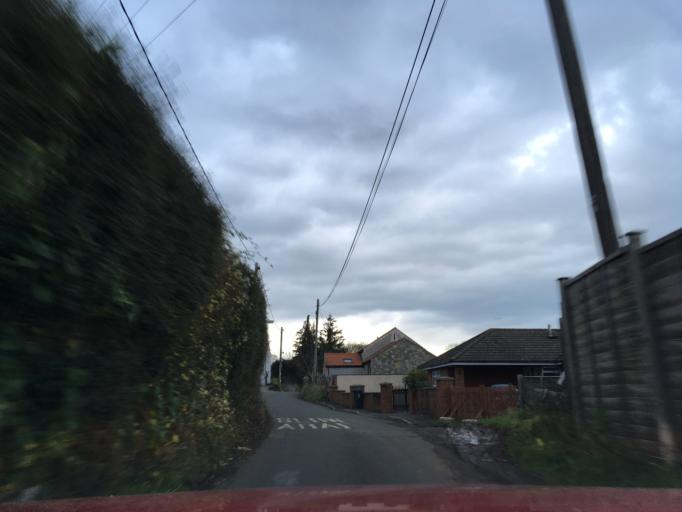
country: GB
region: Wales
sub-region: Newport
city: Bishton
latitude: 51.5862
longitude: -2.8779
